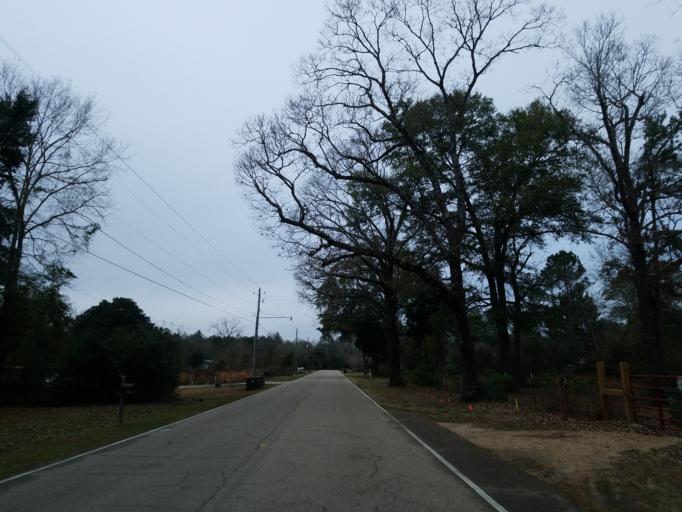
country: US
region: Mississippi
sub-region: Forrest County
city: Hattiesburg
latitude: 31.2858
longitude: -89.2588
